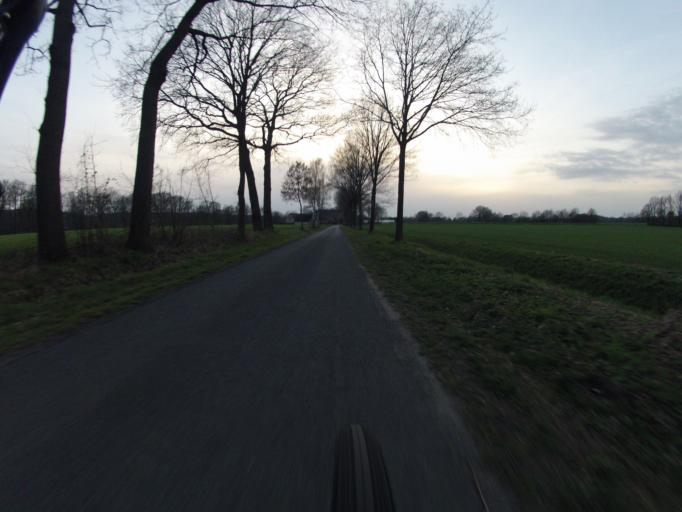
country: DE
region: North Rhine-Westphalia
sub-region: Regierungsbezirk Munster
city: Tecklenburg
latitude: 52.2476
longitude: 7.7659
